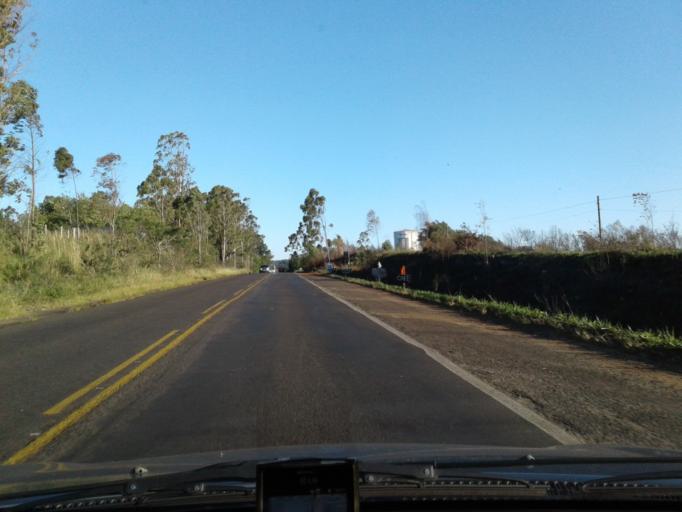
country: BR
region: Rio Grande do Sul
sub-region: Gravatai
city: Gravatai
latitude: -30.0036
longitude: -50.9931
